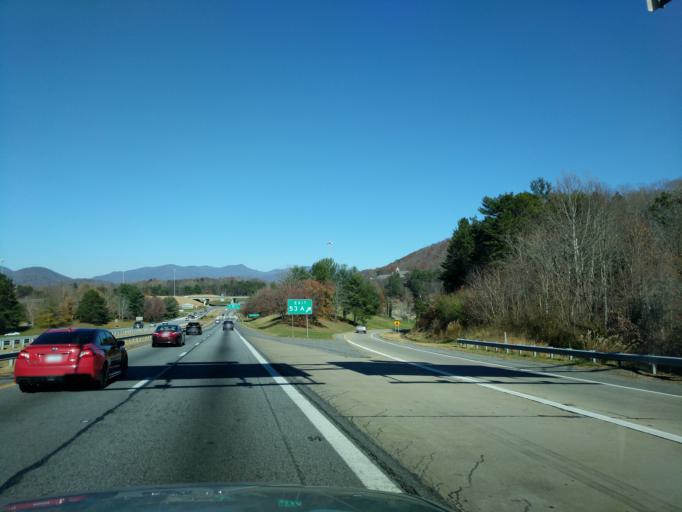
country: US
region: North Carolina
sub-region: Buncombe County
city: Biltmore Forest
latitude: 35.5617
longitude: -82.5008
